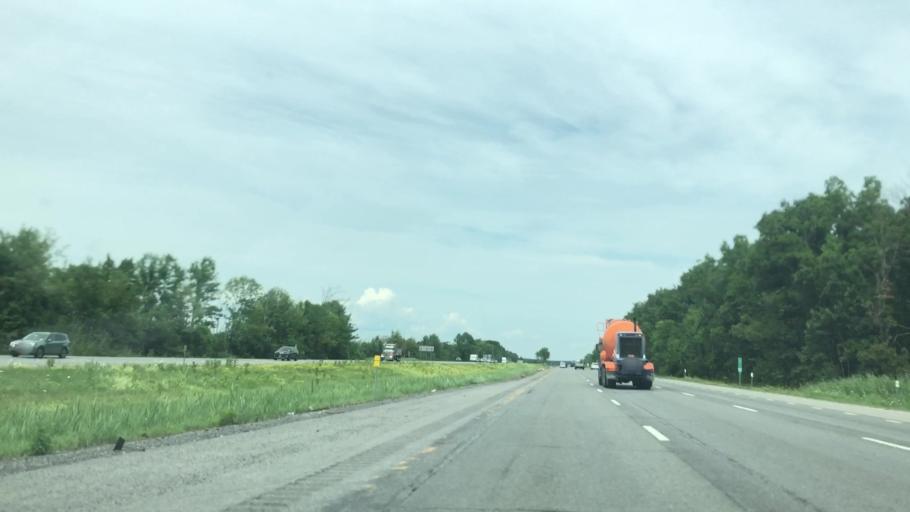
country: US
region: New York
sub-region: Saratoga County
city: Ballston Spa
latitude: 42.9750
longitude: -73.8021
